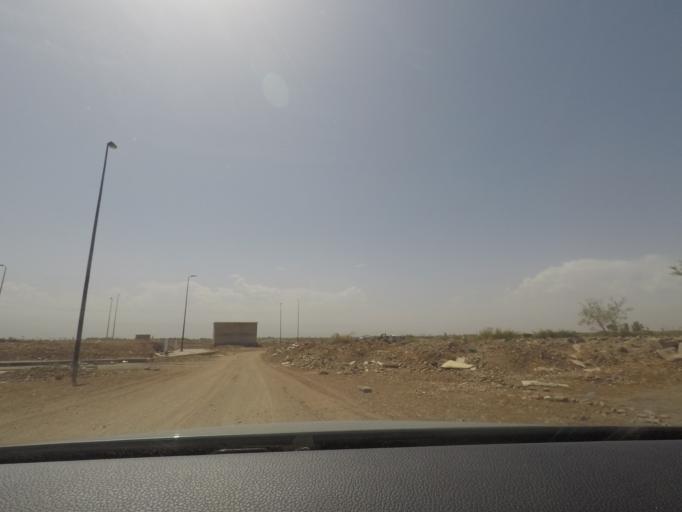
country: MA
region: Marrakech-Tensift-Al Haouz
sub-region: Marrakech
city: Marrakesh
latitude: 31.5825
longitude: -8.0390
